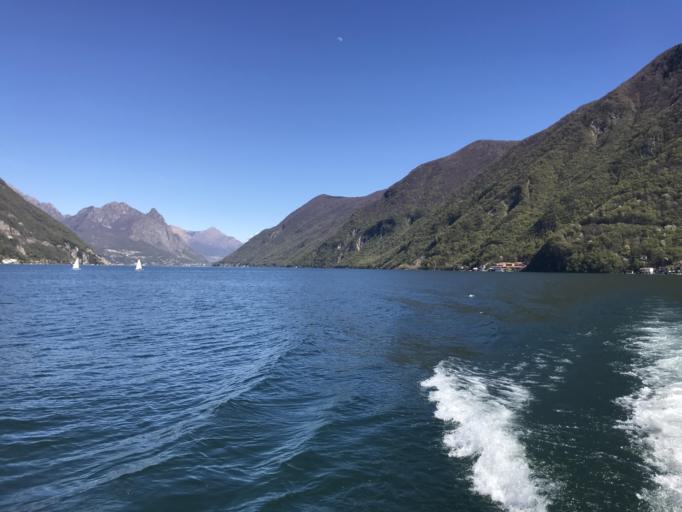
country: IT
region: Lombardy
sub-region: Provincia di Como
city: Campione
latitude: 45.9885
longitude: 8.9658
